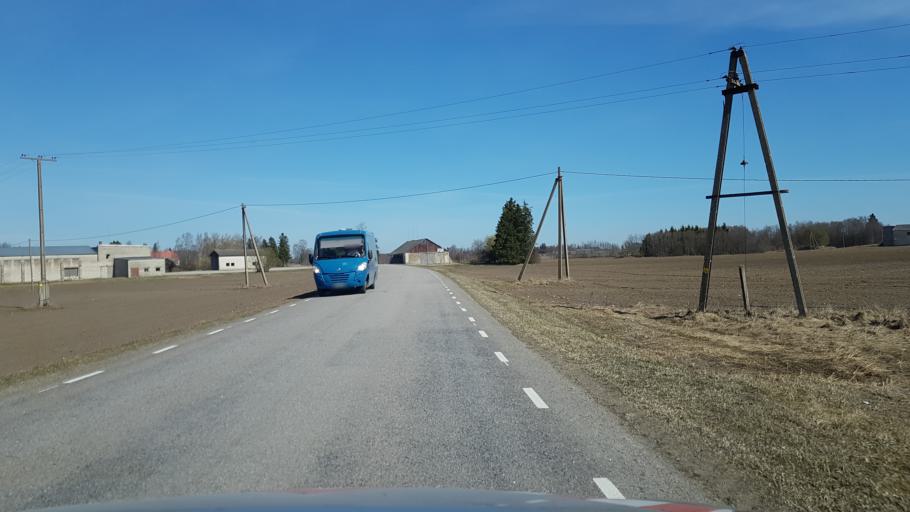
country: EE
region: Laeaene-Virumaa
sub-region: Vinni vald
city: Vinni
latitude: 59.2252
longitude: 26.3411
